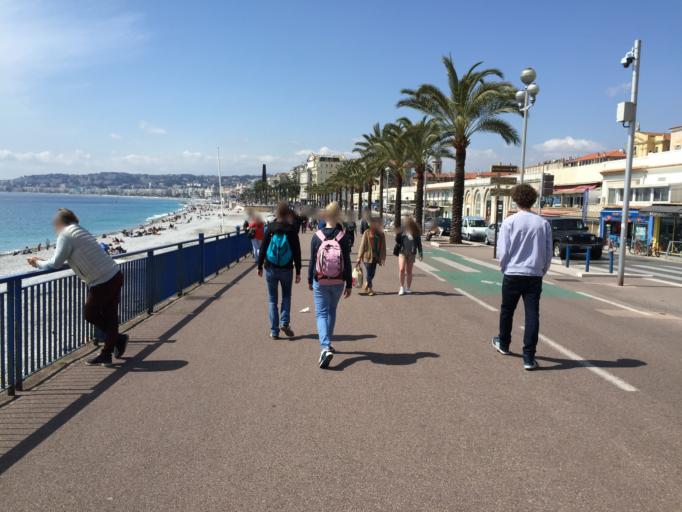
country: FR
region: Provence-Alpes-Cote d'Azur
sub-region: Departement des Alpes-Maritimes
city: Nice
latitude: 43.6948
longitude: 7.2771
